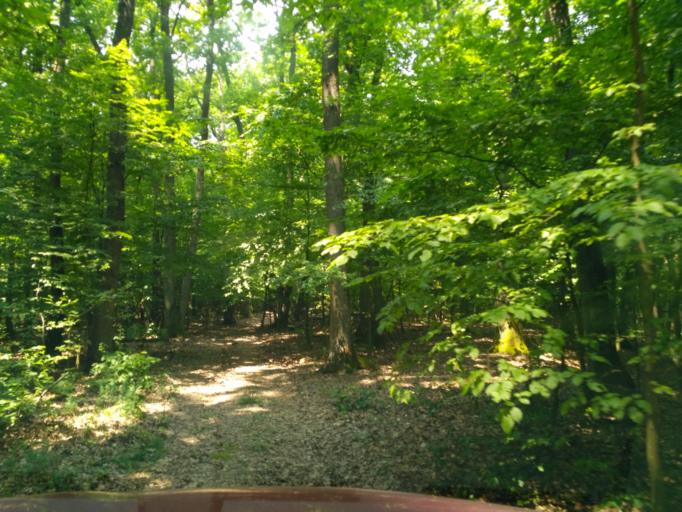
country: SK
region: Kosicky
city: Moldava nad Bodvou
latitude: 48.6468
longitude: 21.0367
